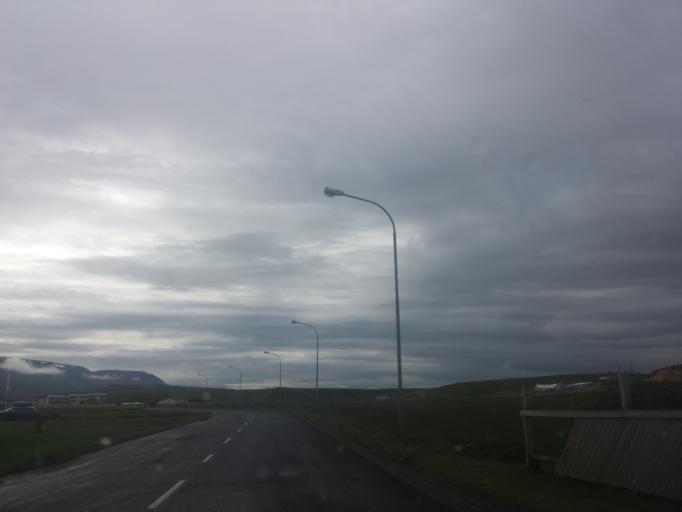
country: IS
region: Northwest
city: Saudarkrokur
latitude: 65.6594
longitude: -20.2998
